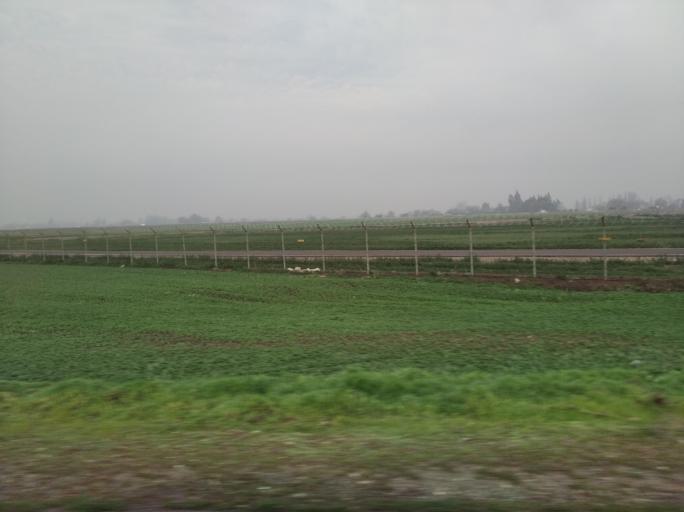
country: CL
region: Santiago Metropolitan
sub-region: Provincia de Santiago
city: Lo Prado
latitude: -33.3670
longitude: -70.7996
